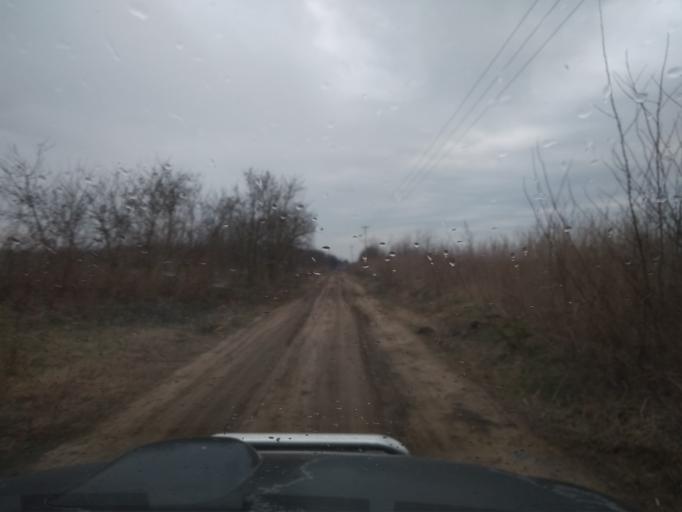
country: HU
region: Szabolcs-Szatmar-Bereg
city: Nyirpazony
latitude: 48.0032
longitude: 21.7888
